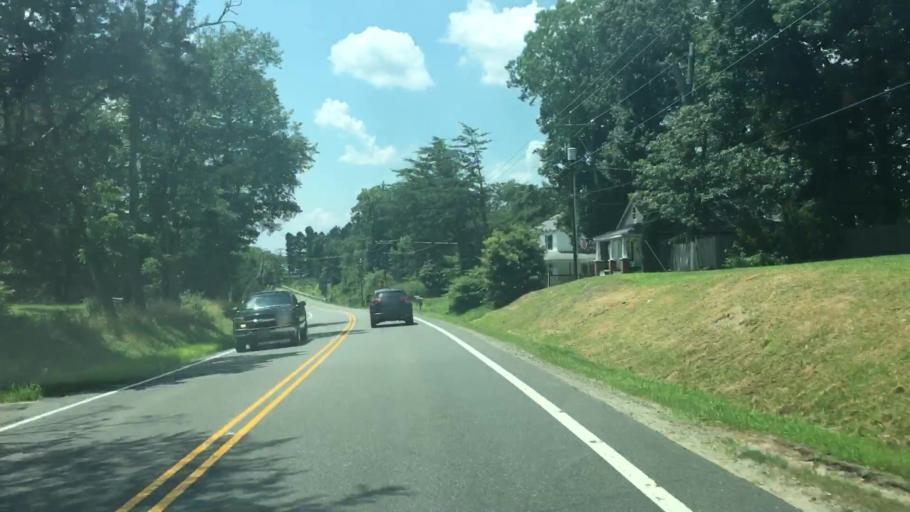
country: US
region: Virginia
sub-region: City of Fredericksburg
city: Fredericksburg
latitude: 38.3119
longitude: -77.4048
